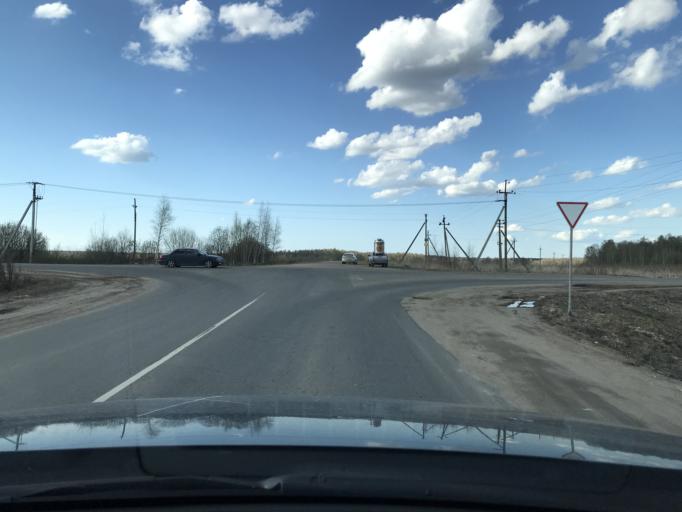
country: RU
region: Vladimir
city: Strunino
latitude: 56.4168
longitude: 38.5857
